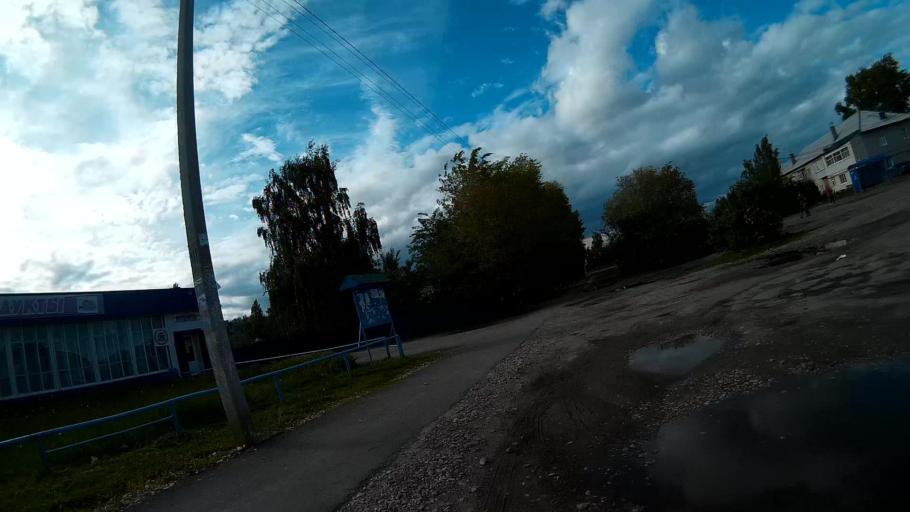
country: RU
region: Ulyanovsk
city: Novoul'yanovsk
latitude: 54.2040
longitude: 48.2663
